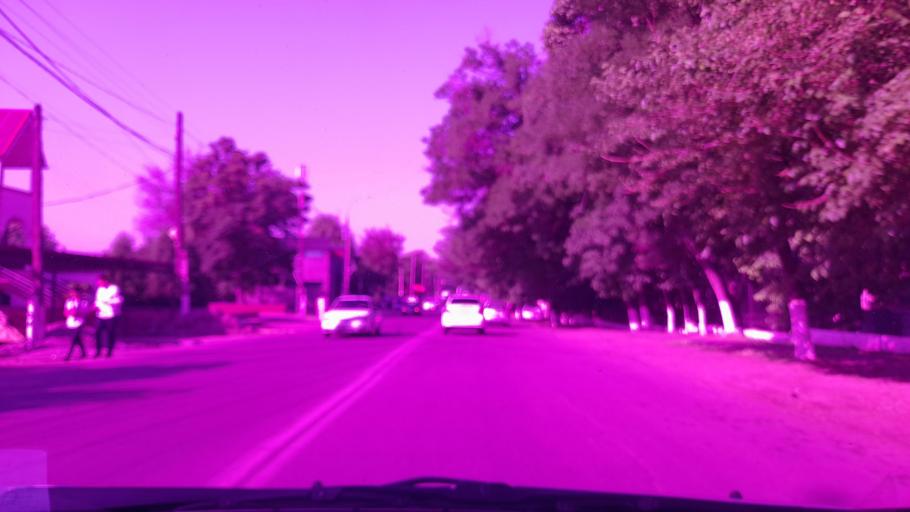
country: UZ
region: Toshkent
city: Salor
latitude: 41.3219
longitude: 69.3449
